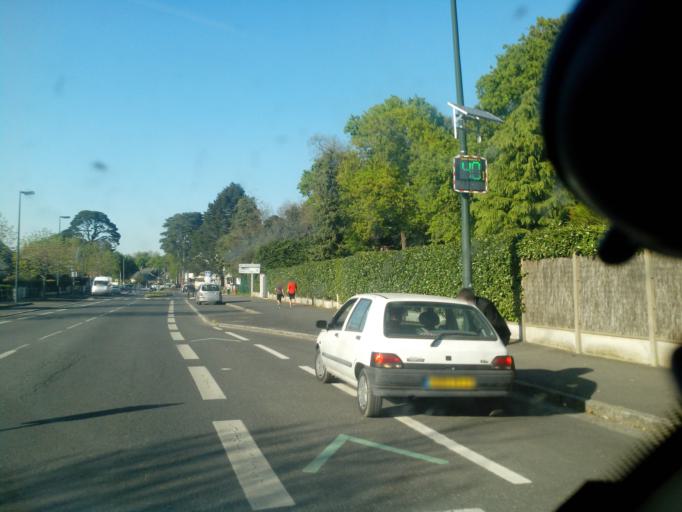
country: FR
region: Pays de la Loire
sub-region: Departement de la Loire-Atlantique
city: Orvault
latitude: 47.2522
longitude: -1.5979
